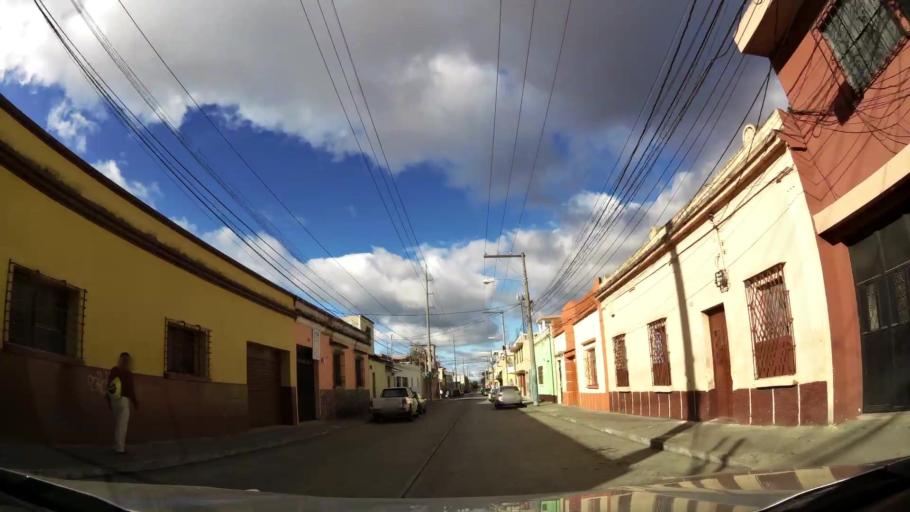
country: GT
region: Guatemala
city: Guatemala City
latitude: 14.6346
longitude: -90.5046
